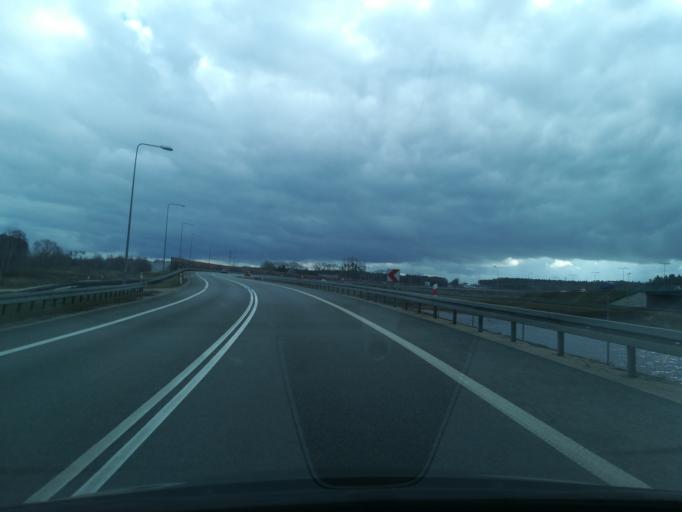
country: PL
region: Kujawsko-Pomorskie
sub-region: Powiat aleksandrowski
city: Ciechocinek
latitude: 52.8679
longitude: 18.7598
